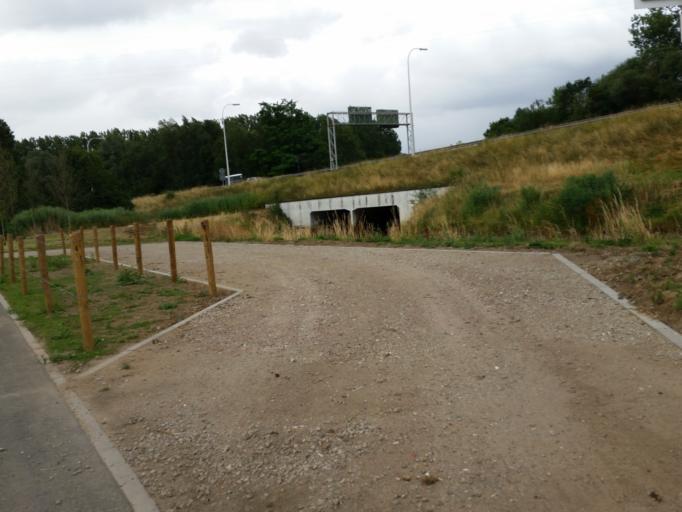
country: BE
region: Flanders
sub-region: Provincie Antwerpen
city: Mechelen
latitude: 51.0487
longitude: 4.4599
